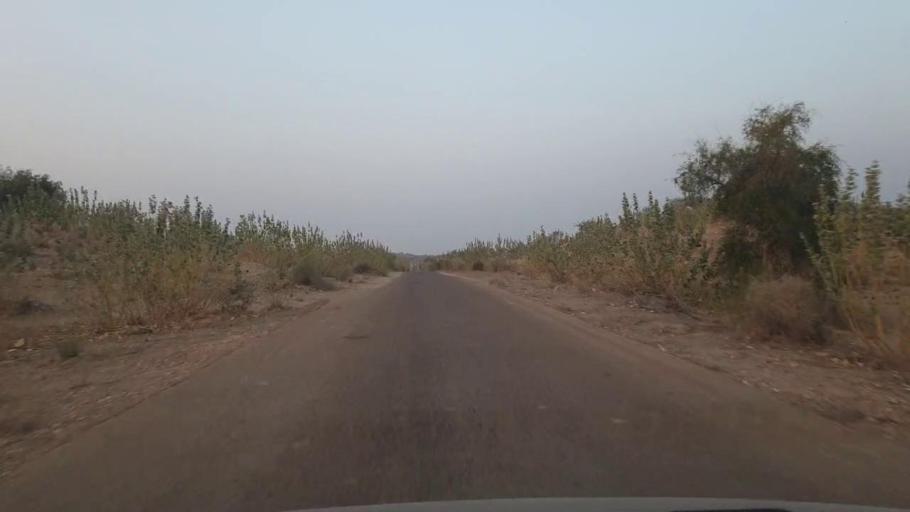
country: PK
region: Sindh
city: Umarkot
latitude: 25.3264
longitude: 70.0576
